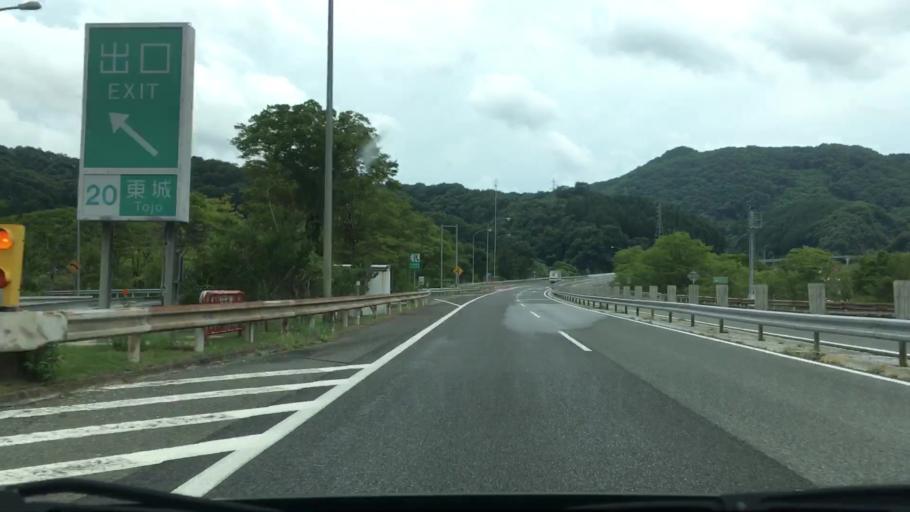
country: JP
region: Okayama
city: Niimi
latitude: 34.8891
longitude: 133.2806
